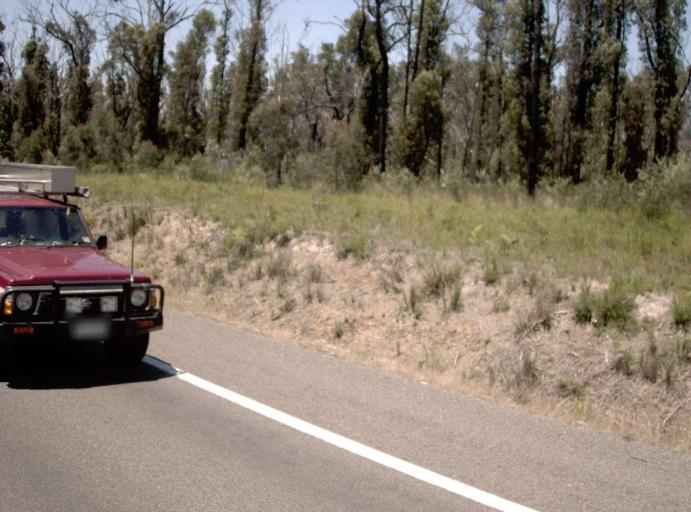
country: AU
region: Victoria
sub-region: East Gippsland
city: Lakes Entrance
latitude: -37.7519
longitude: 148.2159
